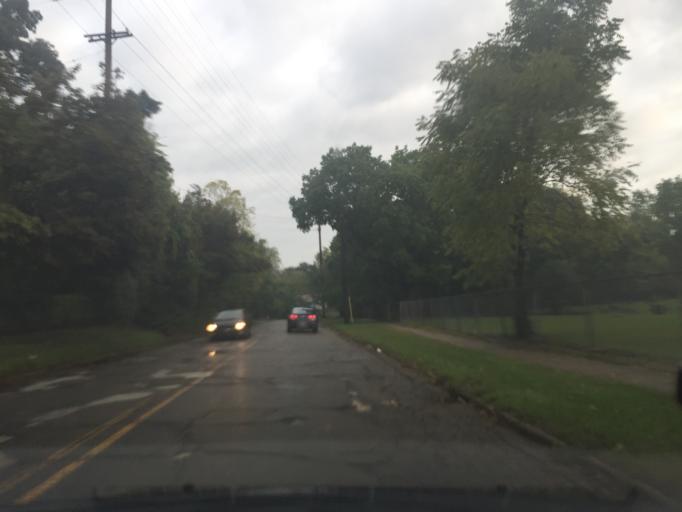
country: US
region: Michigan
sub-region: Oakland County
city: Pontiac
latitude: 42.6442
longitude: -83.2845
